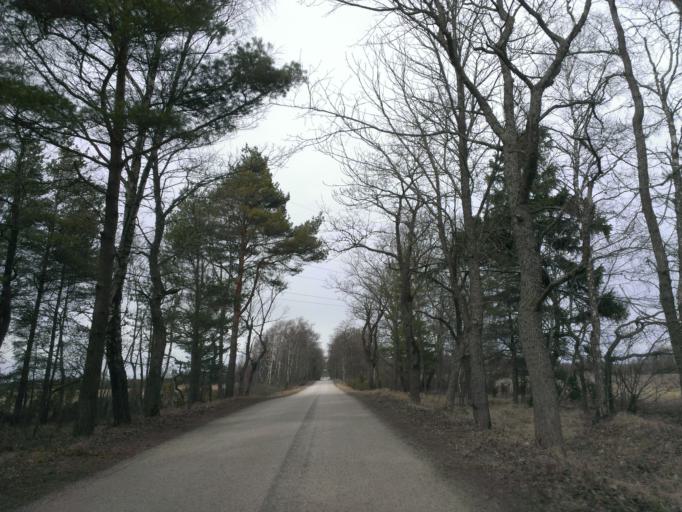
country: EE
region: Laeaene
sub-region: Lihula vald
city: Lihula
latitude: 58.5855
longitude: 23.5372
